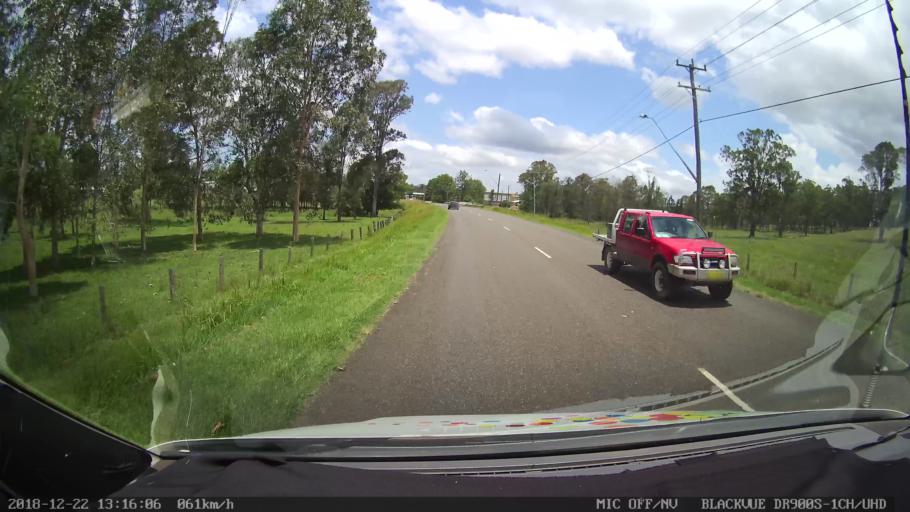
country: AU
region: New South Wales
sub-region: Clarence Valley
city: South Grafton
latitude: -29.7234
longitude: 152.9385
